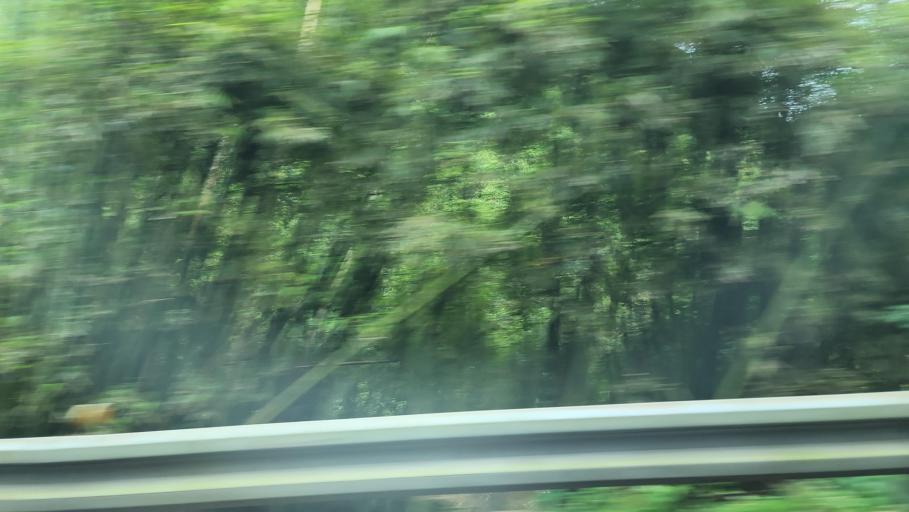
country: TW
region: Taiwan
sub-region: Keelung
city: Keelung
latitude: 25.1623
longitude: 121.6530
